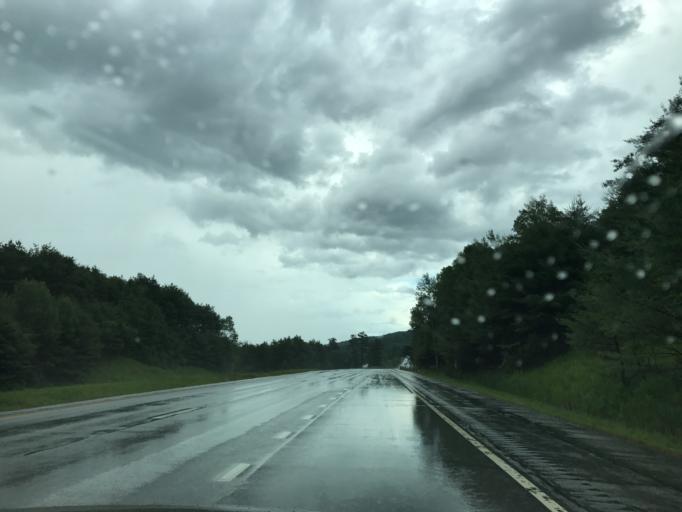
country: US
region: New York
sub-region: Warren County
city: Warrensburg
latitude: 43.4922
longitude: -73.7513
